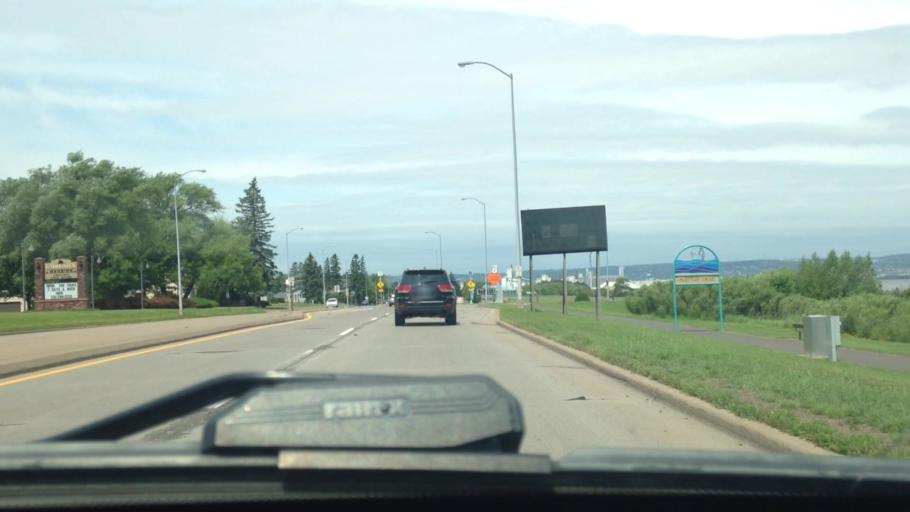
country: US
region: Wisconsin
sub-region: Douglas County
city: Superior
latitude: 46.7180
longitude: -92.0619
